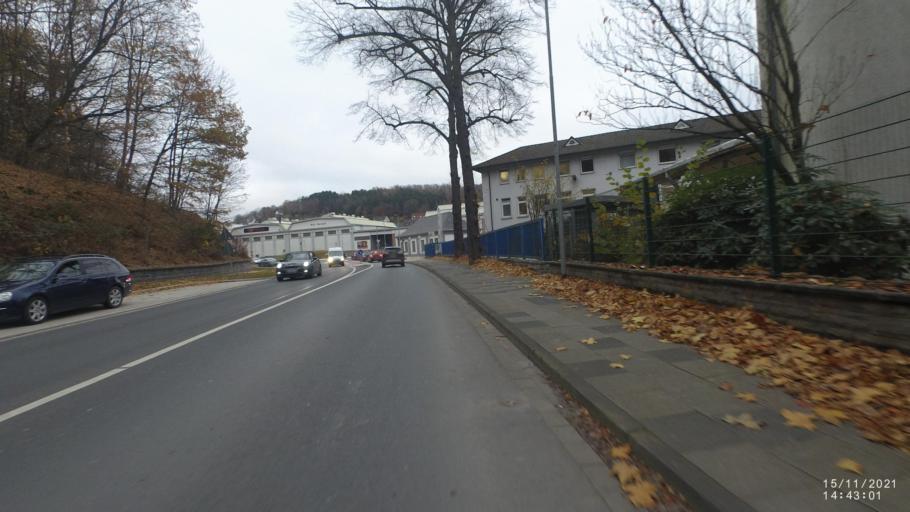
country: DE
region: North Rhine-Westphalia
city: Werdohl
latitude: 51.2543
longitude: 7.7666
